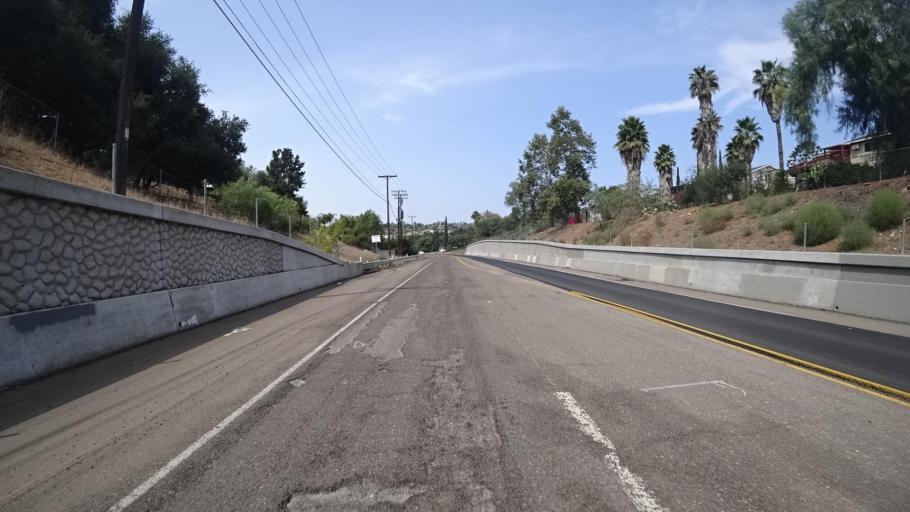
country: US
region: California
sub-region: San Diego County
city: Escondido
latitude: 33.1081
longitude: -117.0465
